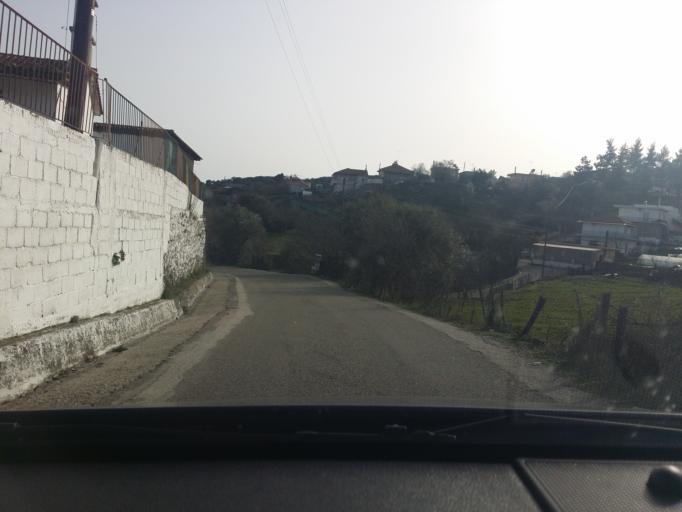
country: GR
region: West Greece
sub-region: Nomos Aitolias kai Akarnanias
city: Katouna
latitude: 38.8238
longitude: 21.0757
